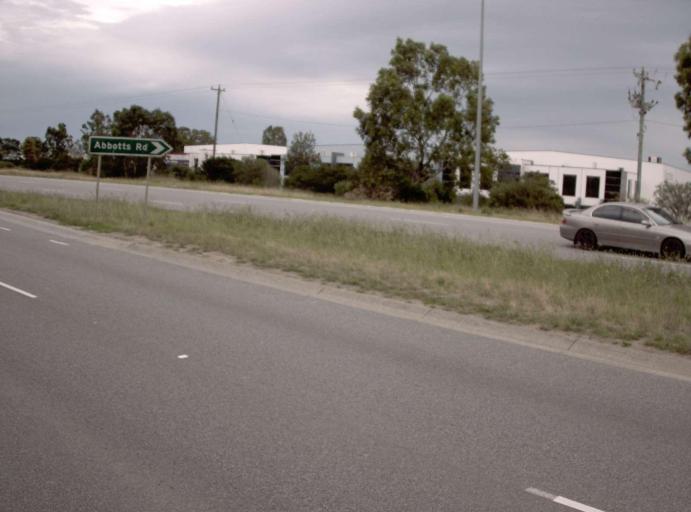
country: AU
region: Victoria
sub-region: Casey
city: Hampton Park
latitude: -38.0331
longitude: 145.2446
